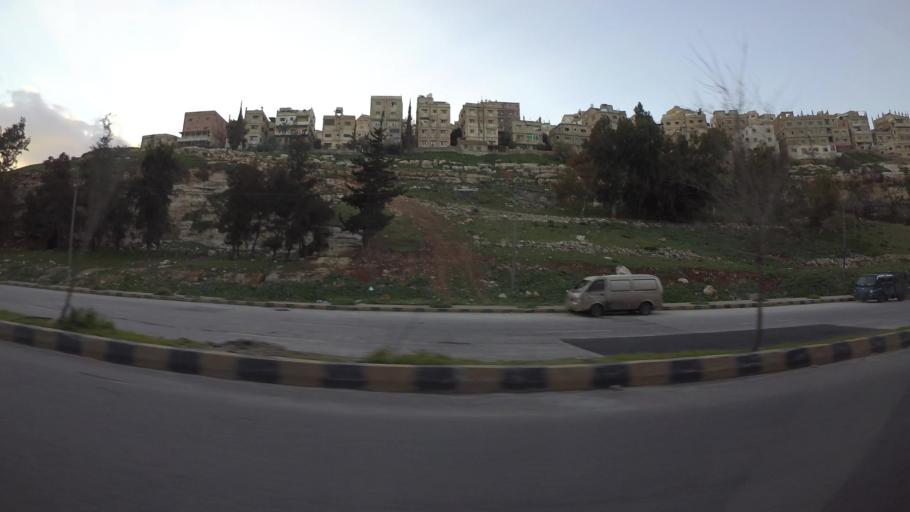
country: JO
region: Amman
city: Al Quwaysimah
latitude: 31.9283
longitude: 35.9193
